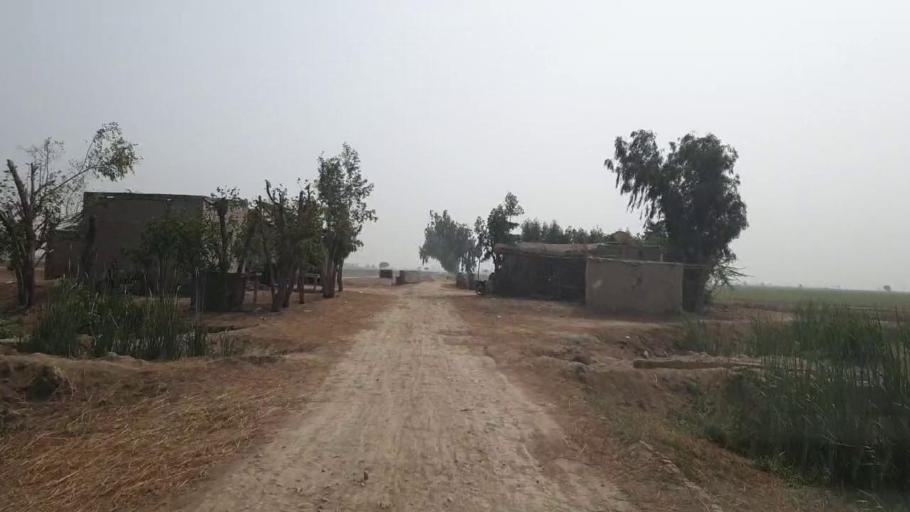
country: PK
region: Sindh
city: Kario
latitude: 24.6322
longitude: 68.5958
